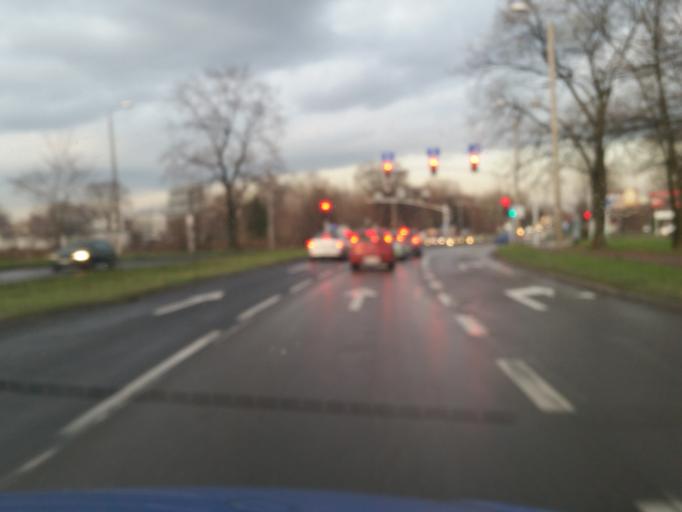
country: PL
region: Silesian Voivodeship
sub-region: Powiat bedzinski
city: Bedzin
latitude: 50.2785
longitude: 19.1746
